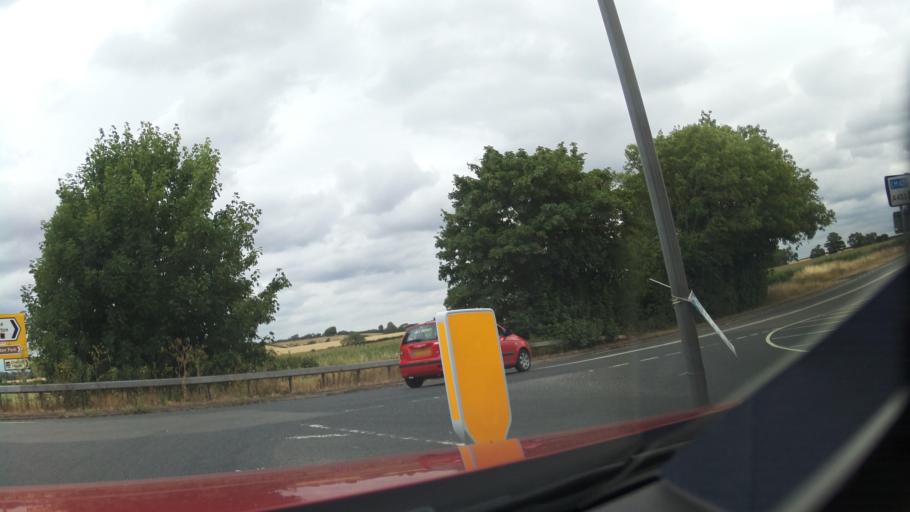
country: GB
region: England
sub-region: Derbyshire
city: Melbourne
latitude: 52.8116
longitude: -1.3806
